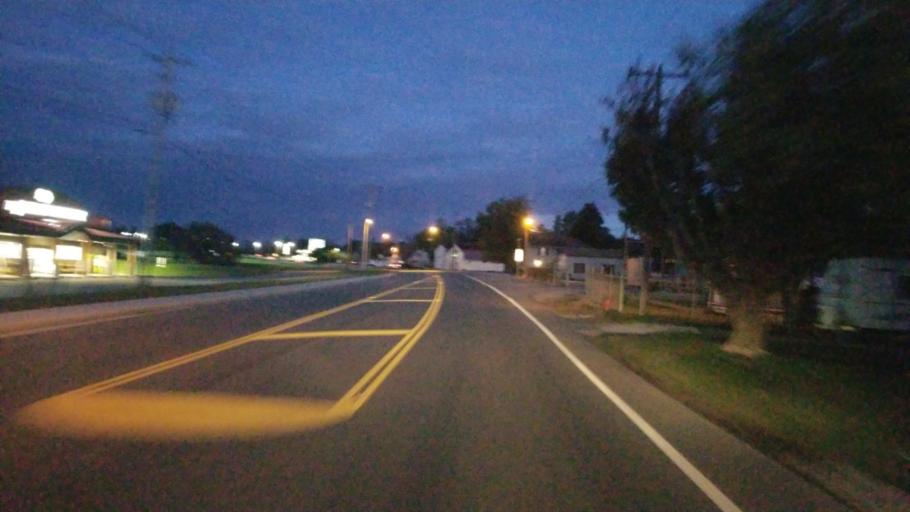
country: US
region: Ohio
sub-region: Vinton County
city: McArthur
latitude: 39.2489
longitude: -82.4884
